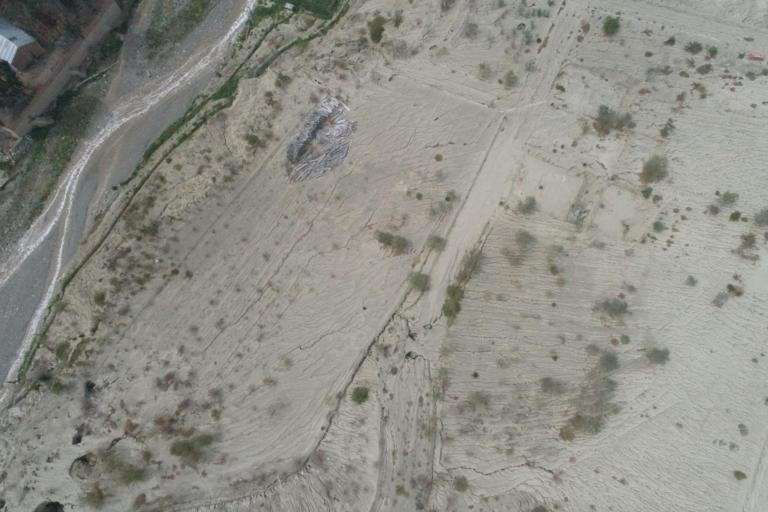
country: BO
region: La Paz
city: La Paz
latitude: -16.6024
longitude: -68.0674
